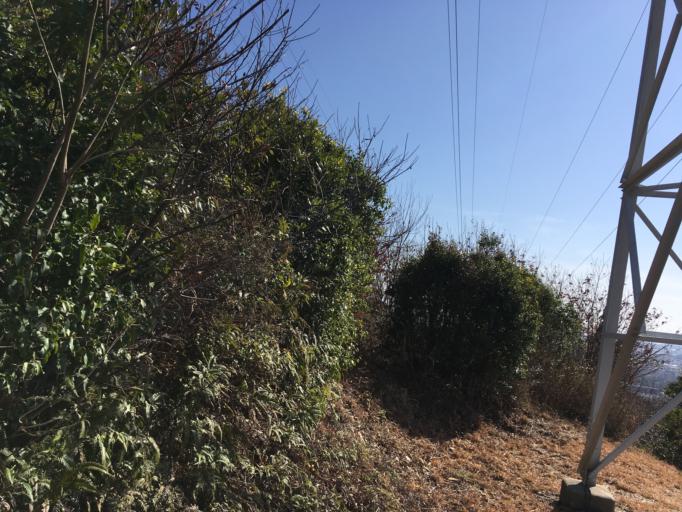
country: JP
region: Aichi
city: Toyohashi
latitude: 34.7369
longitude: 137.4401
